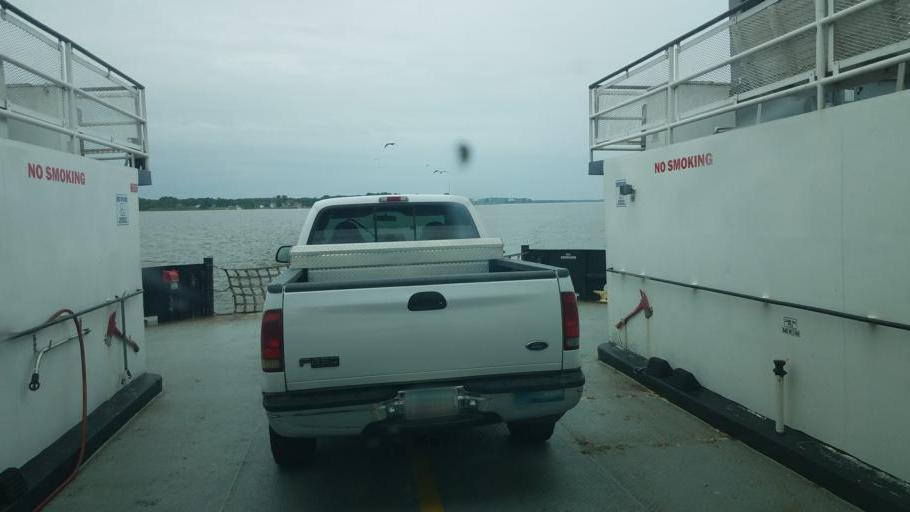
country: US
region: North Carolina
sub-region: Currituck County
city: Currituck
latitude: 36.4787
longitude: -75.9358
